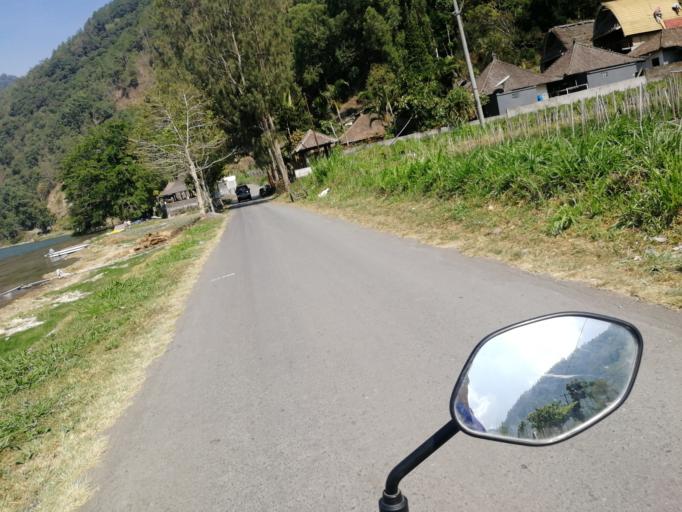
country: ID
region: Bali
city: Banjar Buahan
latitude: -8.2872
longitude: 115.3937
